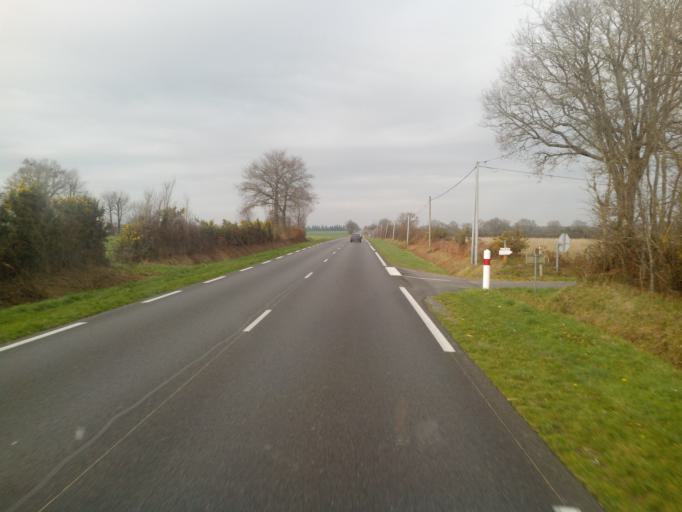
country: FR
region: Poitou-Charentes
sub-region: Departement de la Vienne
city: Saulge
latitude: 46.3034
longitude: 0.8355
